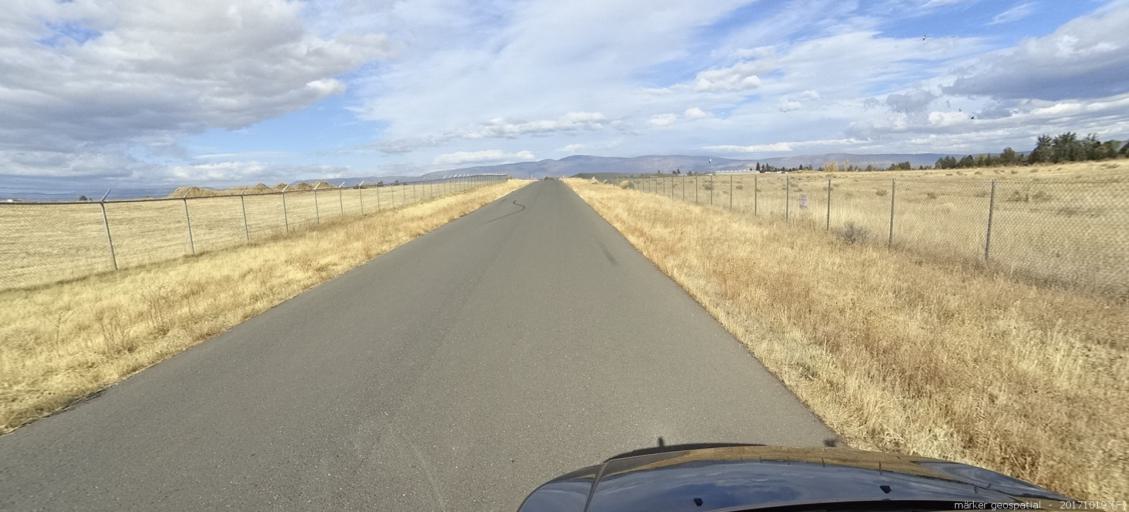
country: US
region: California
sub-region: Shasta County
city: Burney
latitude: 41.0117
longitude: -121.4416
